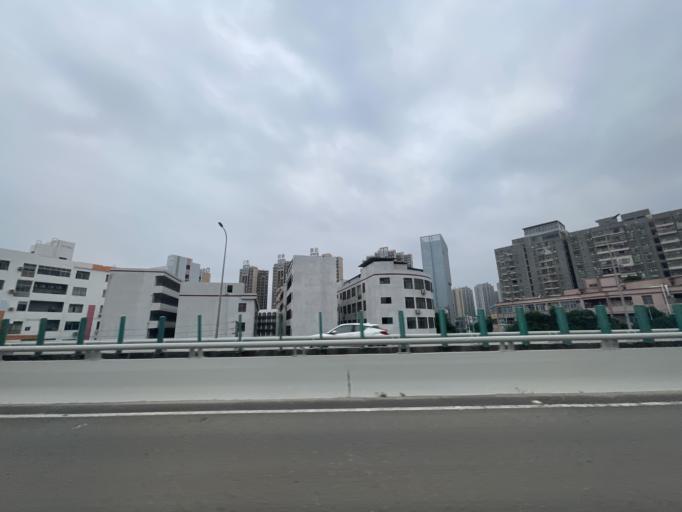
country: CN
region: Guangdong
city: Humen
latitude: 22.8060
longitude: 113.6787
